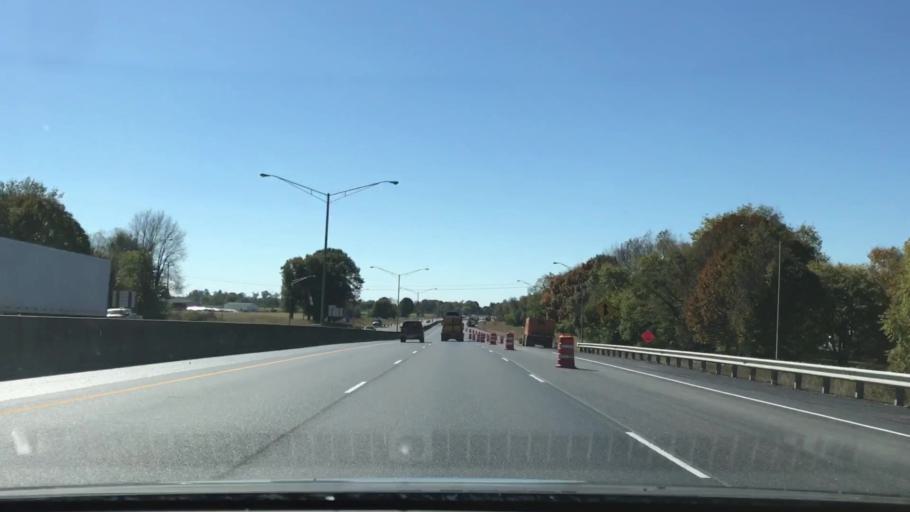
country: US
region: Kentucky
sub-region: Edmonson County
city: Brownsville
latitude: 37.0301
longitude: -86.2424
